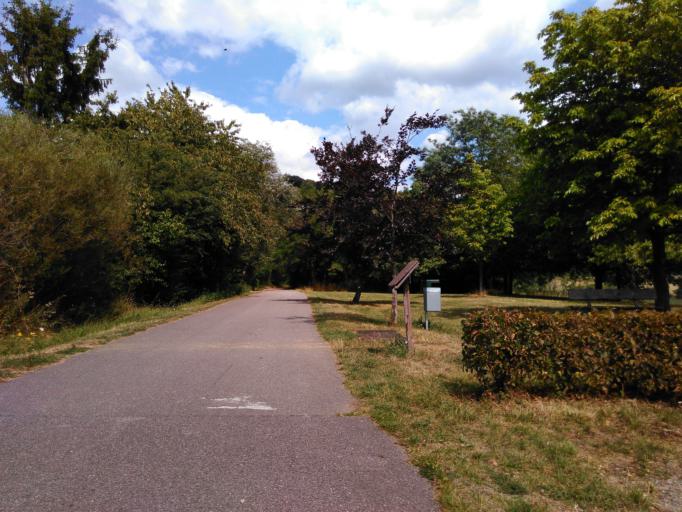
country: LU
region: Grevenmacher
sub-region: Canton d'Echternach
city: Consdorf
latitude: 49.7455
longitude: 6.3329
